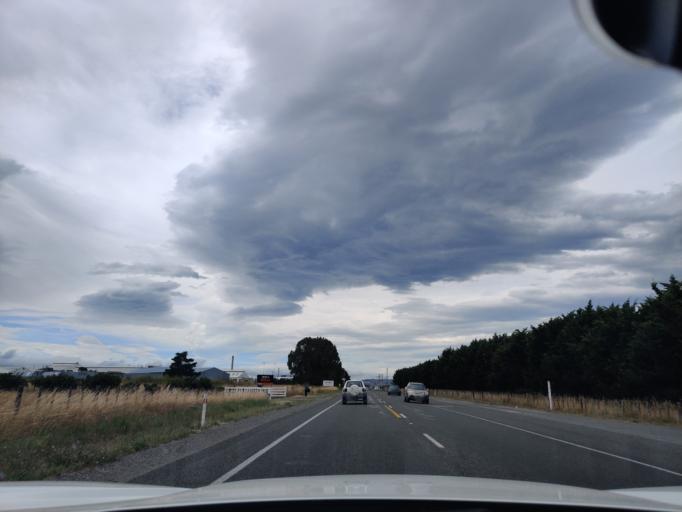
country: NZ
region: Wellington
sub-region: Masterton District
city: Masterton
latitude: -40.9718
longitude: 175.5991
